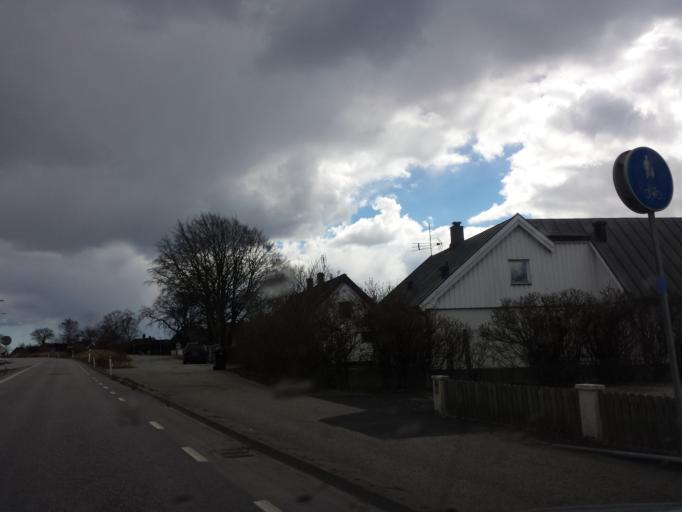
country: SE
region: Skane
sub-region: Ystads Kommun
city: Ystad
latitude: 55.4274
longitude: 13.7220
